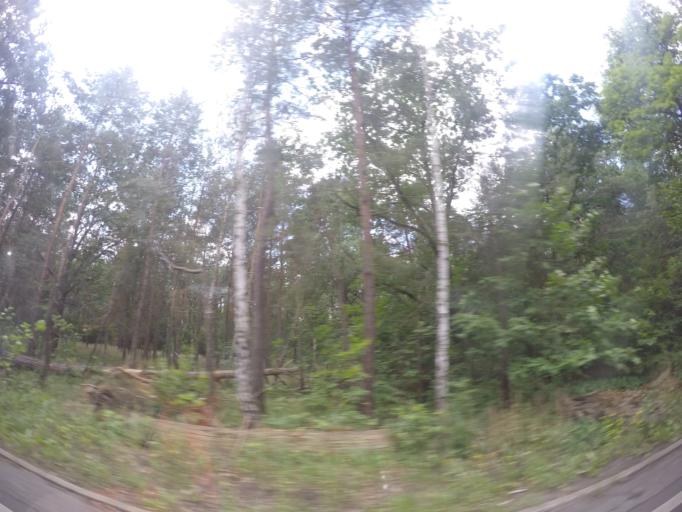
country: DE
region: Berlin
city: Kopenick Bezirk
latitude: 52.4610
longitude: 13.5595
